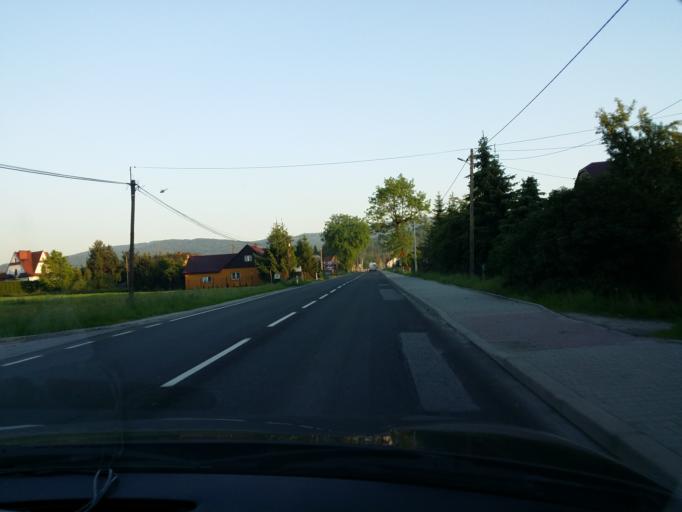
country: PL
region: Lesser Poland Voivodeship
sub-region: Powiat suski
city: Makow Podhalanski
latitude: 49.7159
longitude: 19.6880
